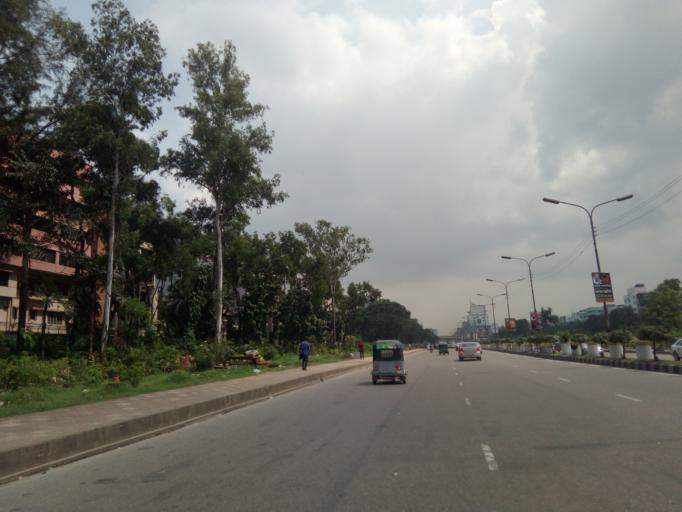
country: BD
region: Dhaka
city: Paltan
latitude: 23.7987
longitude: 90.4018
